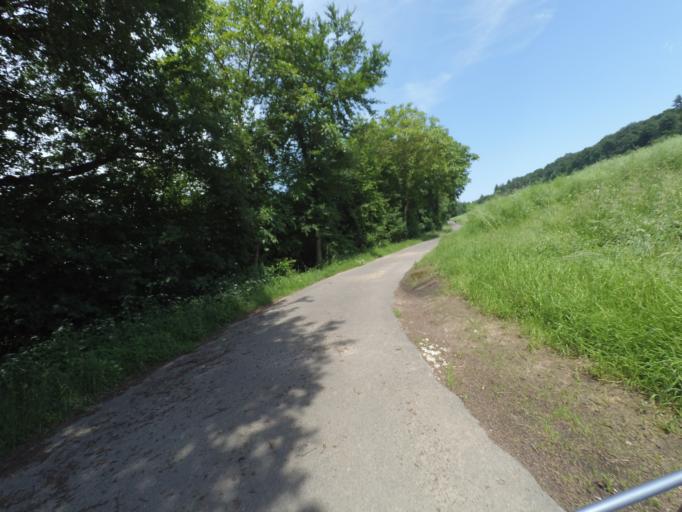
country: DE
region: Rheinland-Pfalz
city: Morshausen
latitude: 50.1939
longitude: 7.4380
